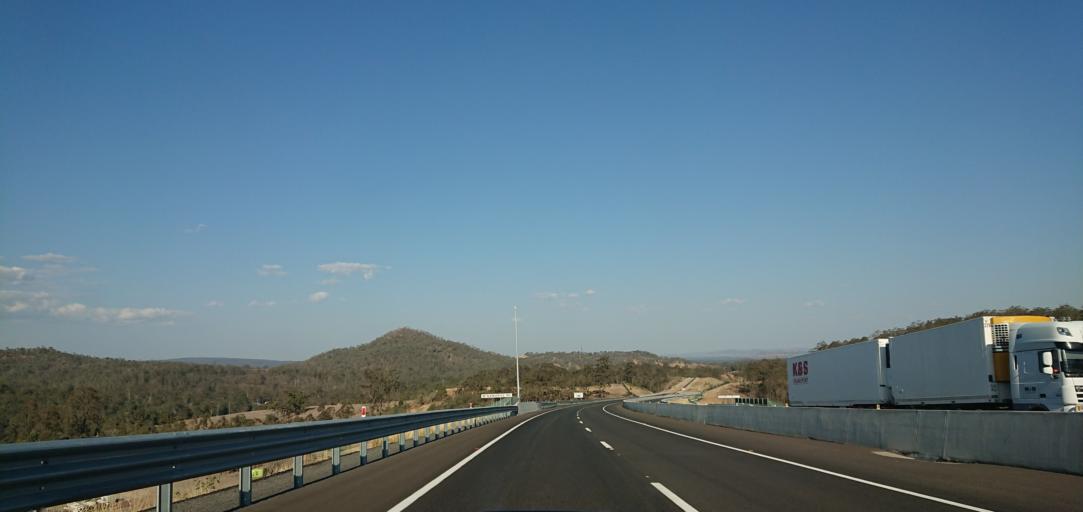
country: AU
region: Queensland
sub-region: Toowoomba
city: East Toowoomba
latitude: -27.5075
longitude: 152.0102
